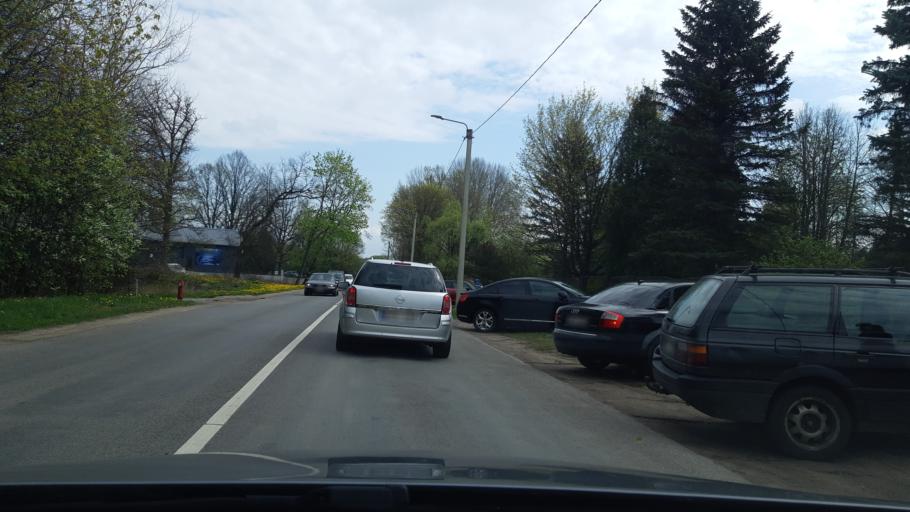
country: LT
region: Kauno apskritis
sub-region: Kaunas
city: Silainiai
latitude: 54.9241
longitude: 23.8519
